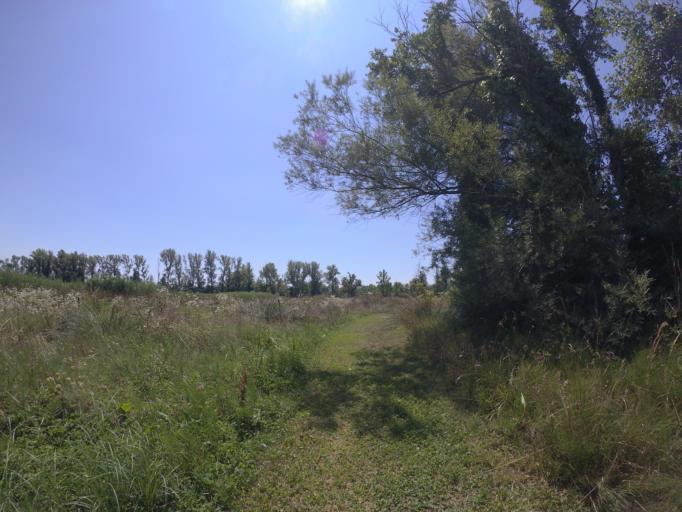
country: IT
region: Friuli Venezia Giulia
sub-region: Provincia di Udine
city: Bertiolo
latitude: 45.9172
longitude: 13.0786
